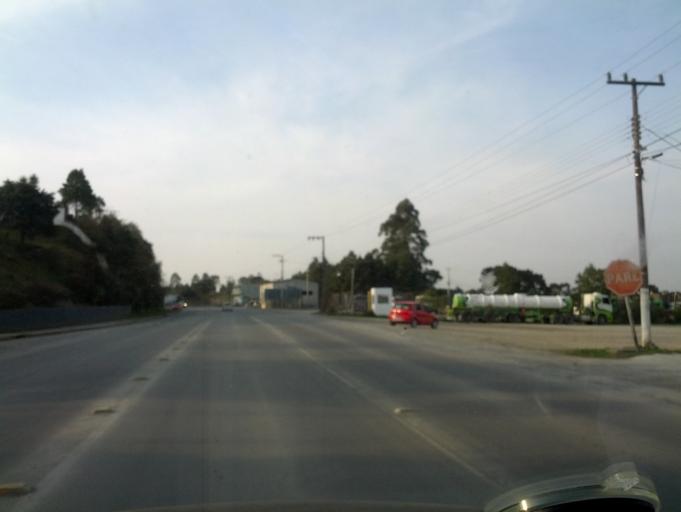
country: BR
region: Santa Catarina
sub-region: Otacilio Costa
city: Otacilio Costa
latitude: -27.4888
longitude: -50.1183
